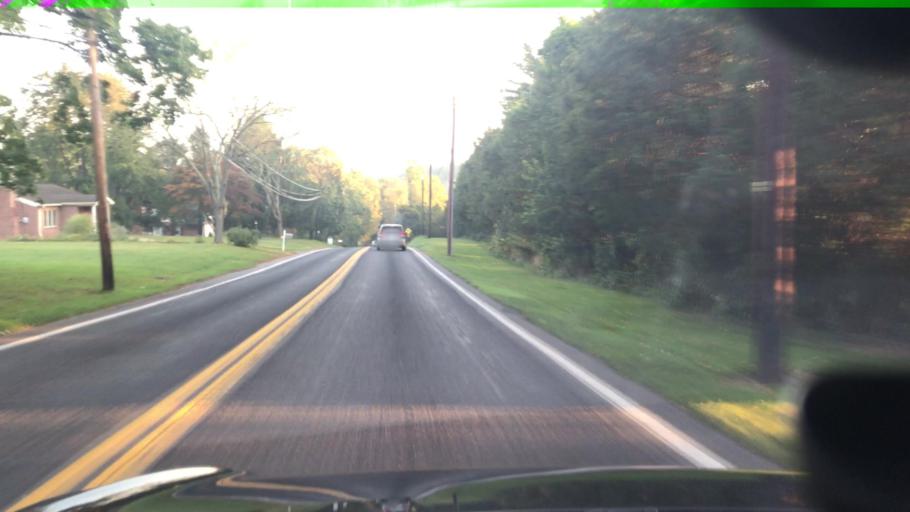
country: US
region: Pennsylvania
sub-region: Cumberland County
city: Lower Allen
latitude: 40.1707
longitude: -76.9208
